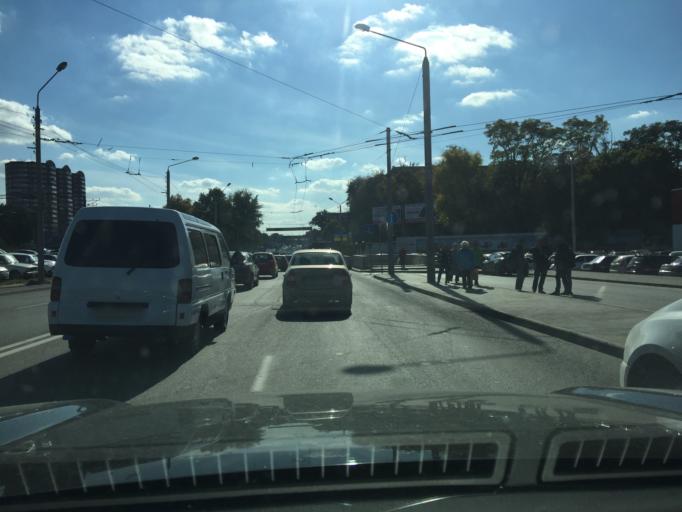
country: RU
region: Rostov
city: Imeni Chkalova
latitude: 47.2582
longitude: 39.7656
